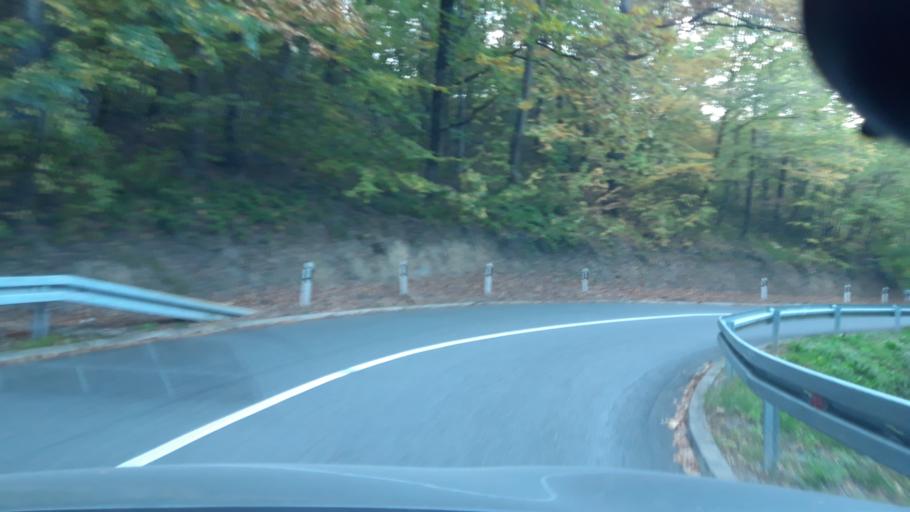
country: RS
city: Vrdnik
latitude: 45.1589
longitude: 19.7763
